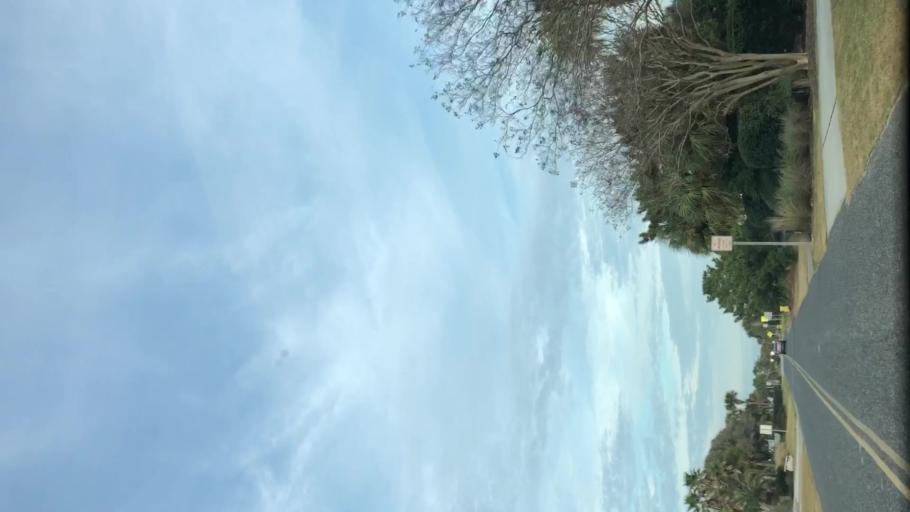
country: US
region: South Carolina
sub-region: Charleston County
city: Isle of Palms
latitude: 32.7774
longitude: -79.8040
